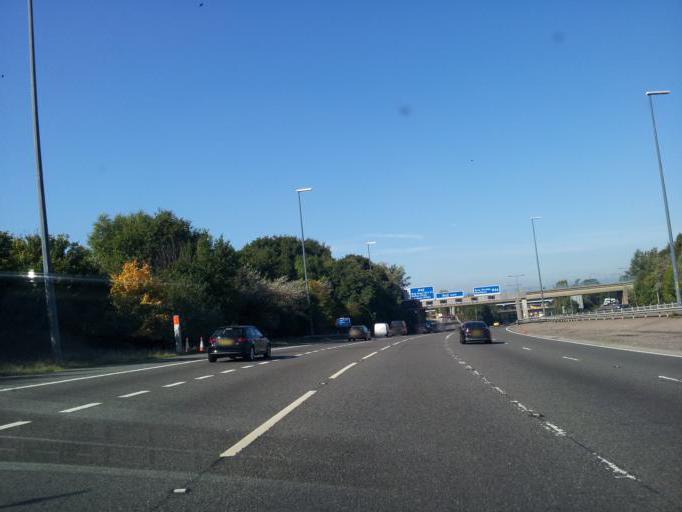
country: GB
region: England
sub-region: Borough of Bury
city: Prestwich
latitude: 53.5464
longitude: -2.2565
